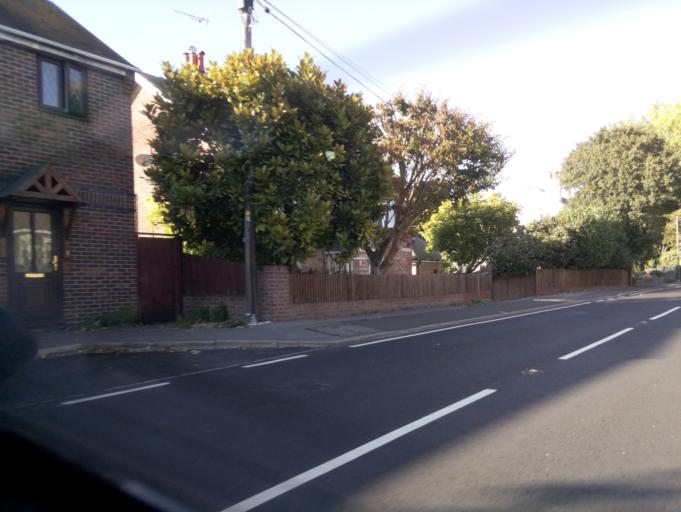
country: GB
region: England
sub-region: Hampshire
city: Swanmore
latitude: 50.9806
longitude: -1.1304
